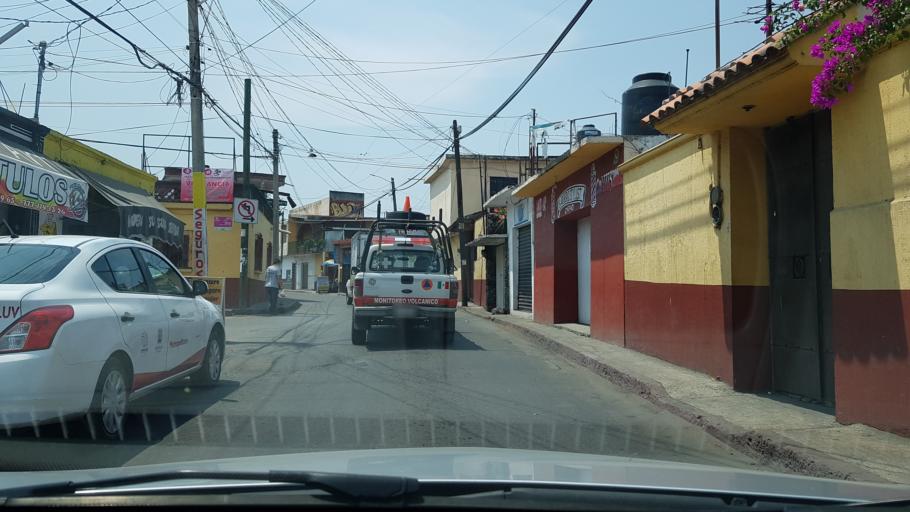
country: MX
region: Morelos
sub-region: Jiutepec
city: Jiutepec
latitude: 18.8802
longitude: -99.1788
